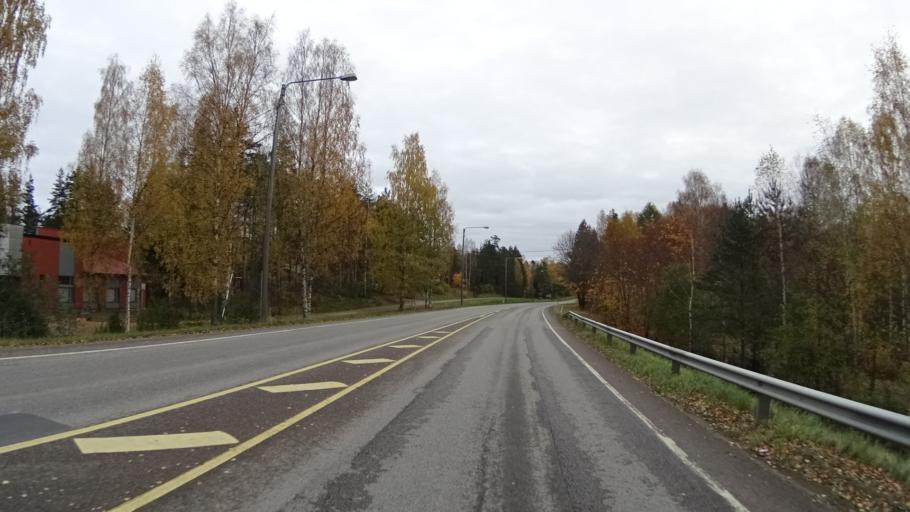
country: FI
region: South Karelia
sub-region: Lappeenranta
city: Lemi
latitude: 60.9585
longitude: 27.7899
